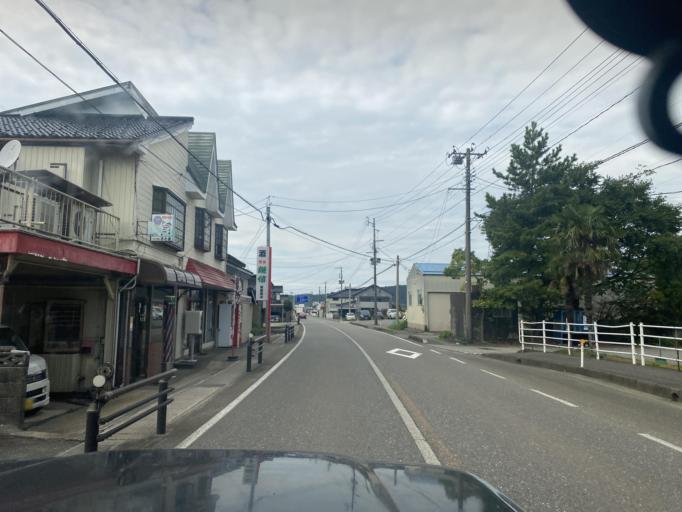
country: JP
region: Niigata
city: Itoigawa
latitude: 37.0017
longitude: 137.8704
